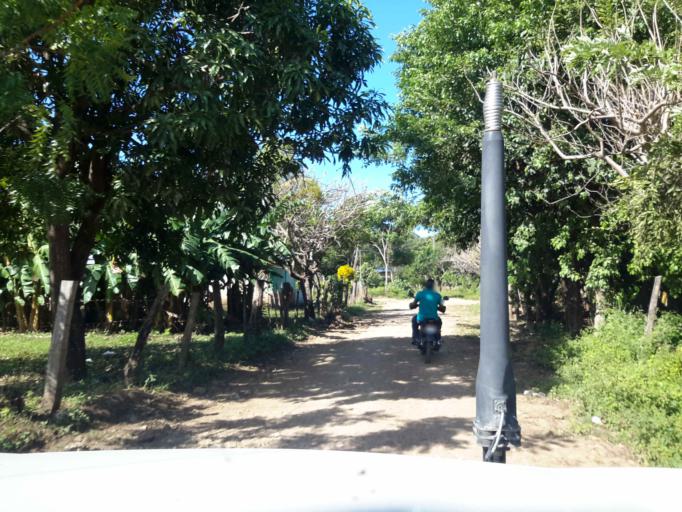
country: NI
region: Rivas
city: Tola
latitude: 11.4630
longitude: -85.9482
